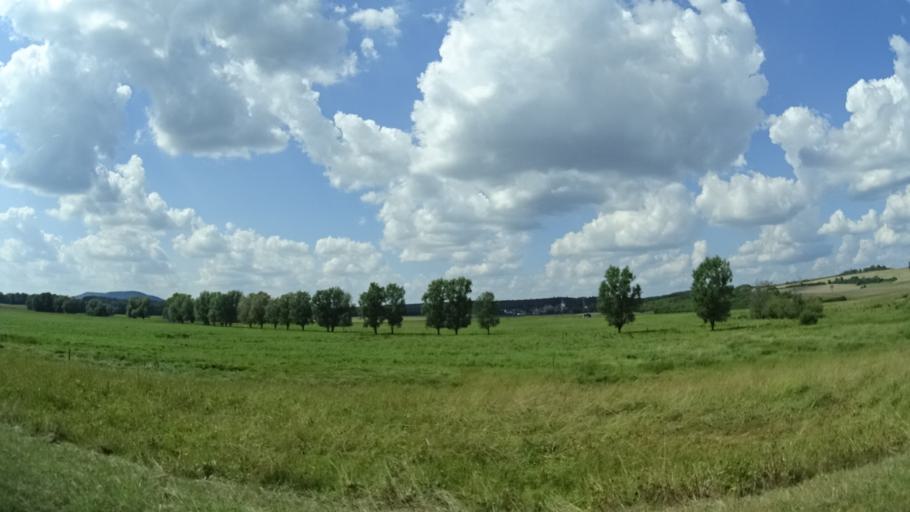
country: DE
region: Thuringia
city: Hildburghausen
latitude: 50.3735
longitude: 10.7115
